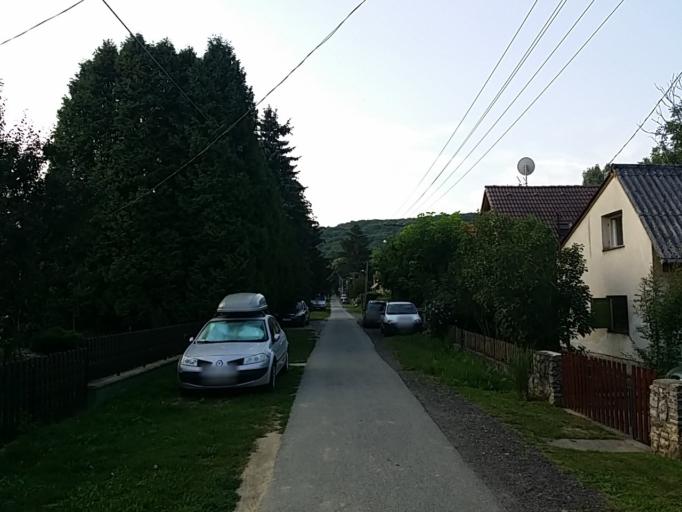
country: HU
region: Baranya
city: Pellerd
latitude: 46.1413
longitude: 18.1160
